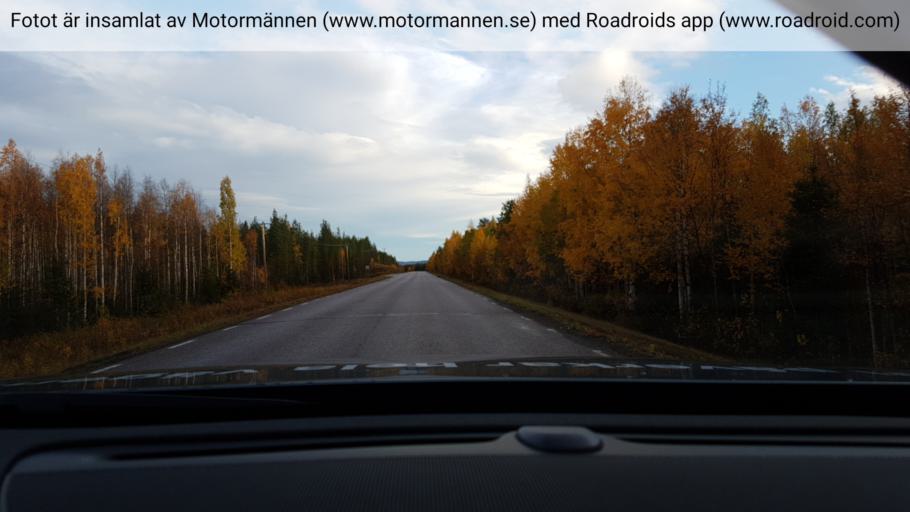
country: SE
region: Norrbotten
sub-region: Overkalix Kommun
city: OEverkalix
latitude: 67.0212
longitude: 22.5196
